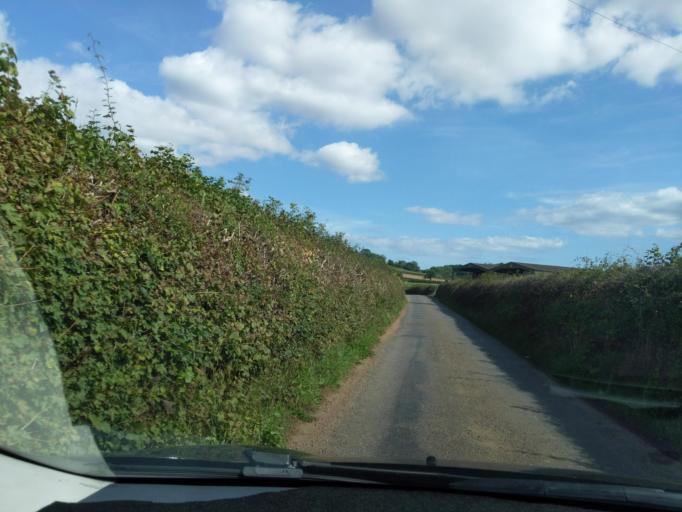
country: GB
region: England
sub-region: Devon
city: Ipplepen
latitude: 50.4617
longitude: -3.6283
